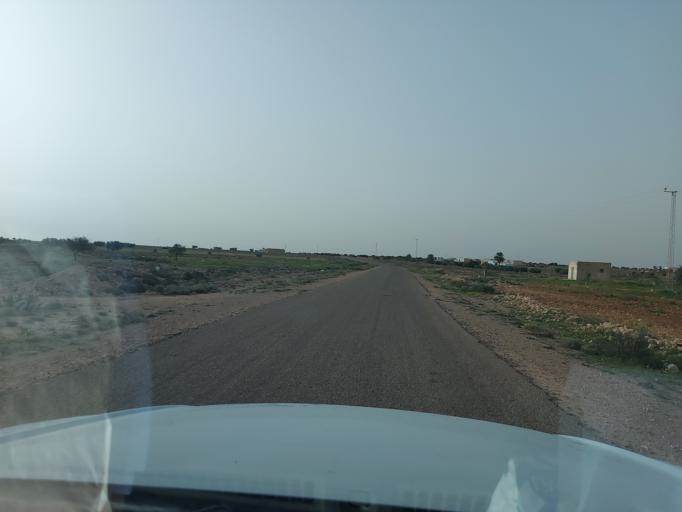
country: TN
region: Madanin
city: Medenine
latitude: 33.3499
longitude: 10.5873
